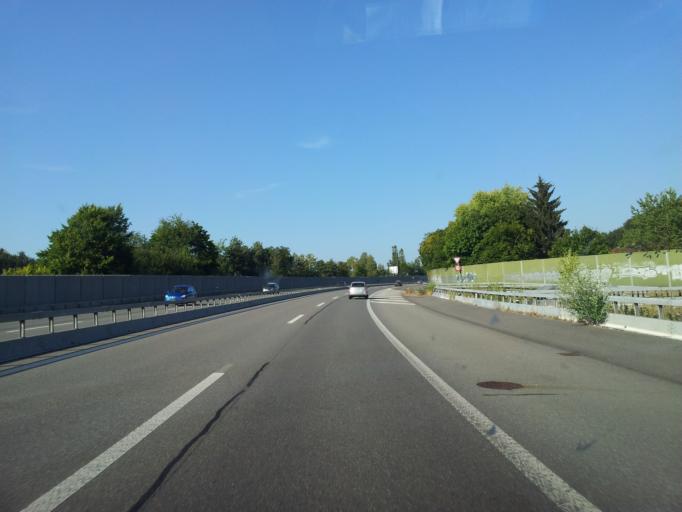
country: CH
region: Bern
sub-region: Bern-Mittelland District
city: Koniz
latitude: 46.9304
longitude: 7.3816
